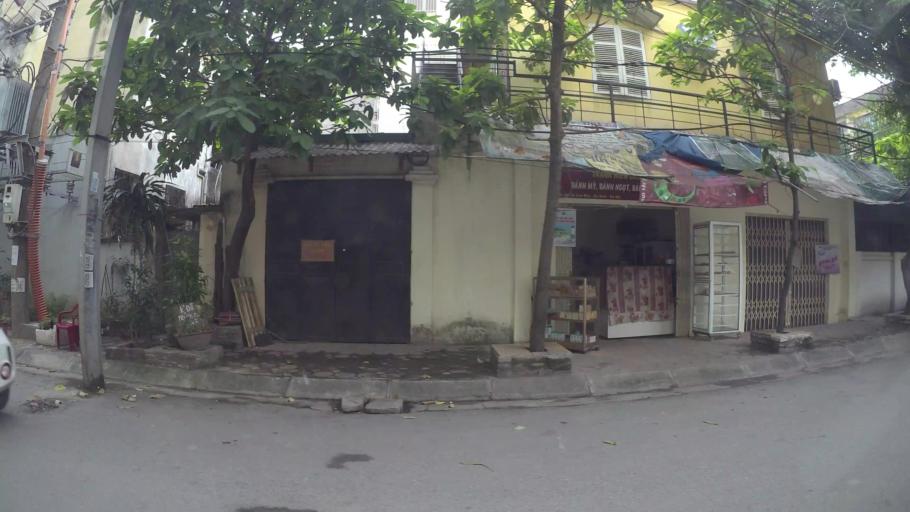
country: VN
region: Ha Noi
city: Cau Giay
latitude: 21.0344
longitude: 105.8163
